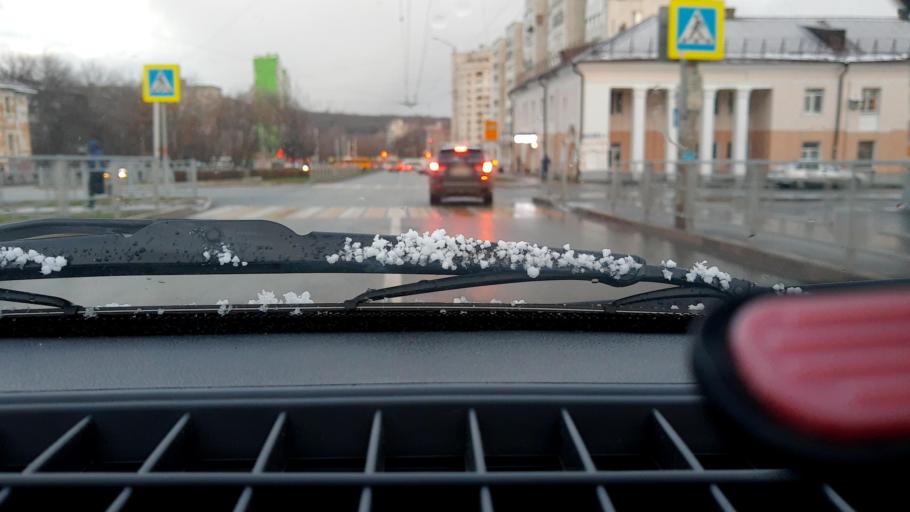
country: RU
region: Bashkortostan
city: Ufa
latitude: 54.8107
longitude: 56.1217
